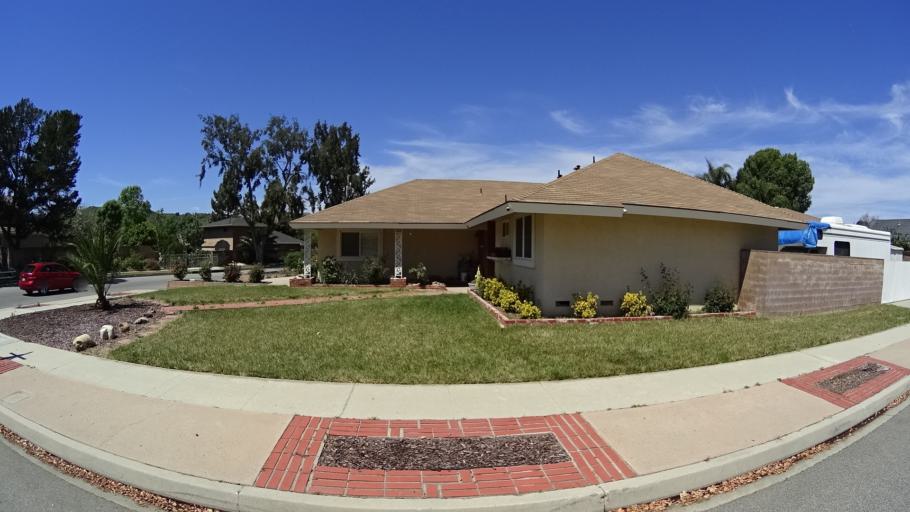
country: US
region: California
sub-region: Ventura County
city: Casa Conejo
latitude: 34.1595
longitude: -118.9546
